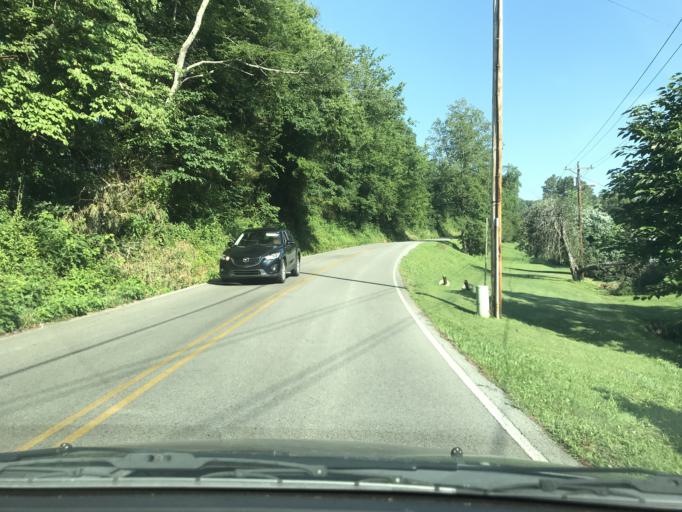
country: US
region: Tennessee
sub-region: Loudon County
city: Loudon
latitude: 35.7816
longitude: -84.3575
